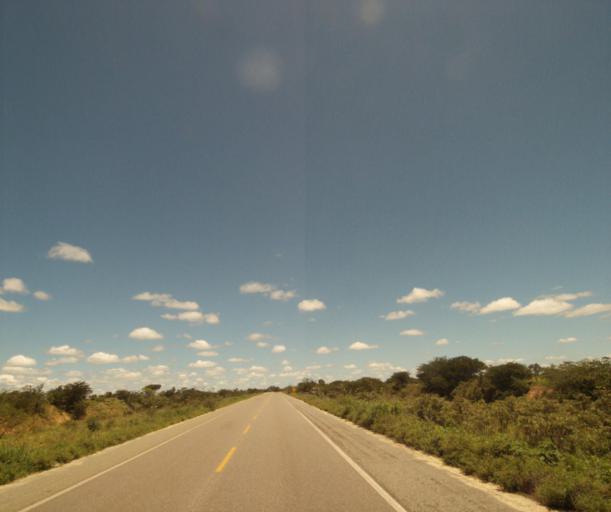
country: BR
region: Bahia
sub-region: Carinhanha
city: Carinhanha
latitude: -14.2938
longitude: -43.7855
